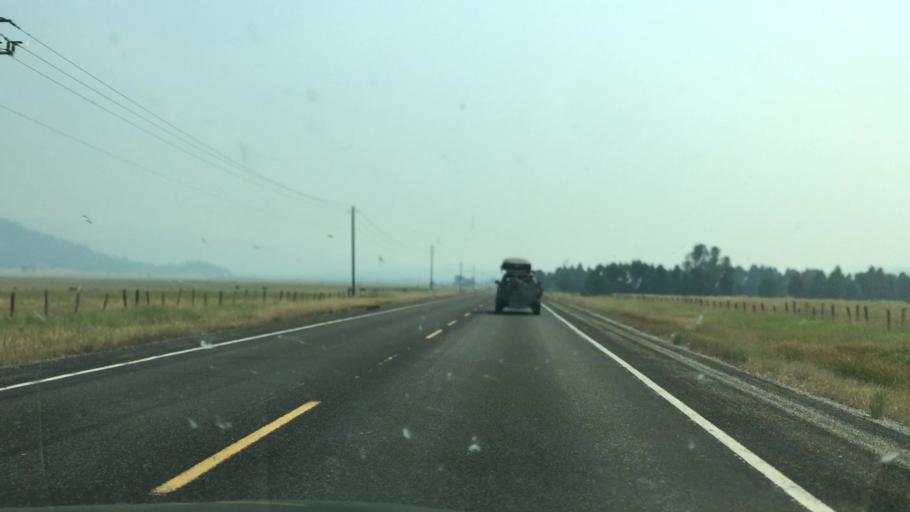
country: US
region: Idaho
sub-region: Valley County
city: Cascade
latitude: 44.4424
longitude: -115.9994
